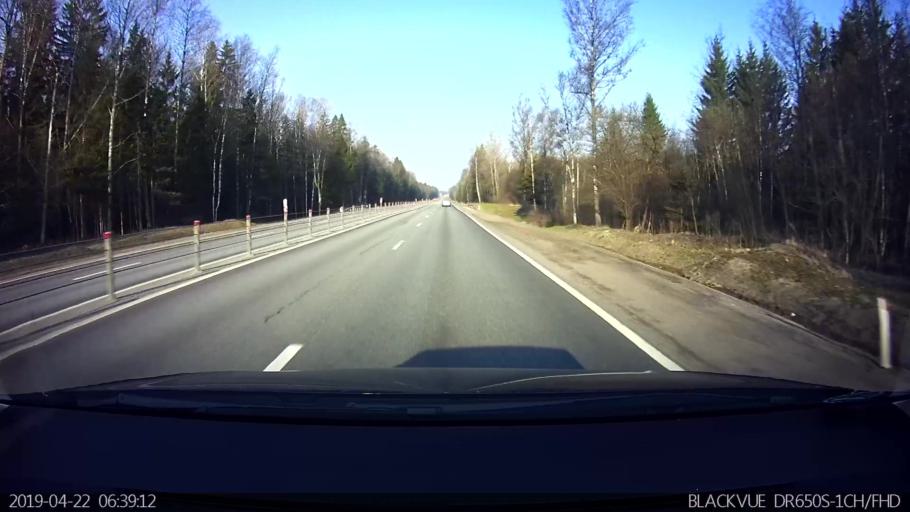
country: RU
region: Moskovskaya
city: Uvarovka
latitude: 55.4915
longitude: 35.3453
